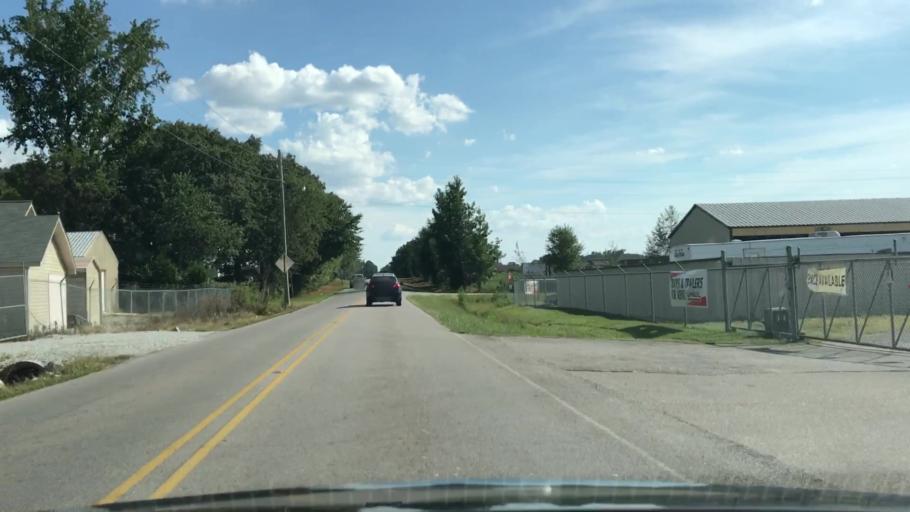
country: US
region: Alabama
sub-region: Madison County
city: Harvest
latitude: 34.8972
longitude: -86.7486
